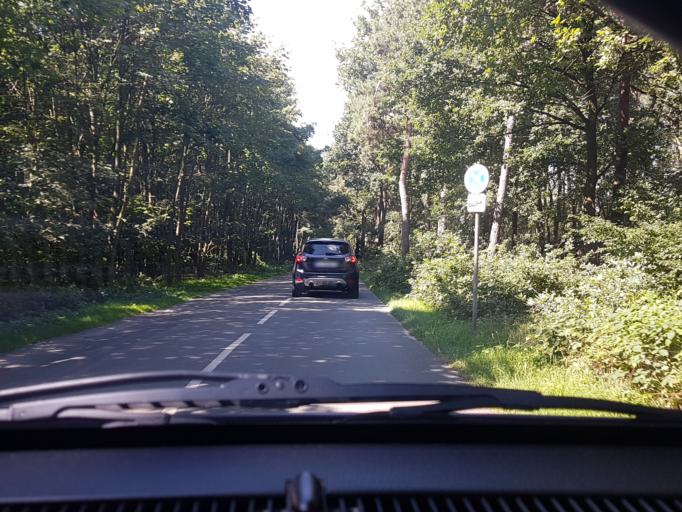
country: DE
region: North Rhine-Westphalia
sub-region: Regierungsbezirk Munster
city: Neuenkirchen
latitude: 52.2322
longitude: 7.3509
